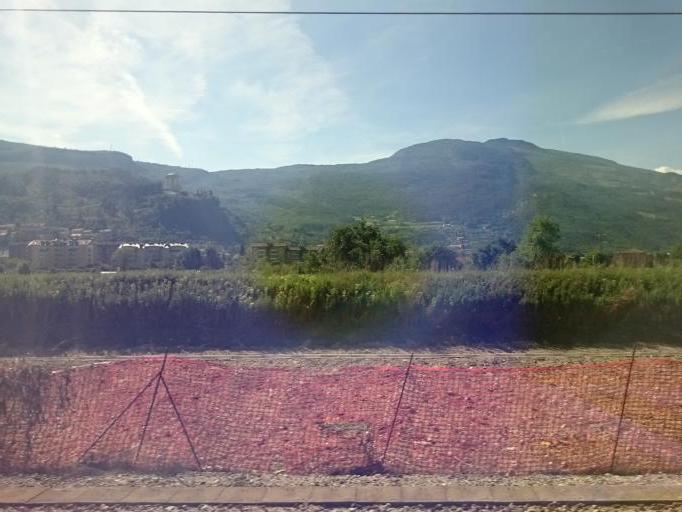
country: IT
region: Trentino-Alto Adige
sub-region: Provincia di Trento
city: Rovereto
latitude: 45.8758
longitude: 11.0241
